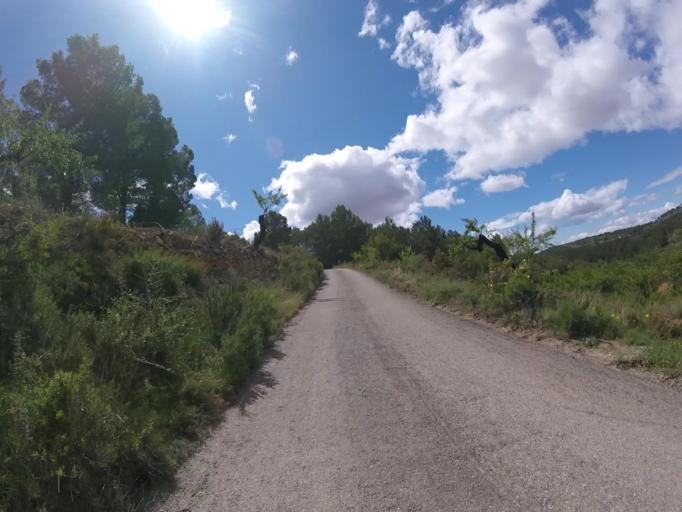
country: ES
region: Valencia
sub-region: Provincia de Castello
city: Sierra-Engarceran
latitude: 40.2711
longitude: -0.0978
